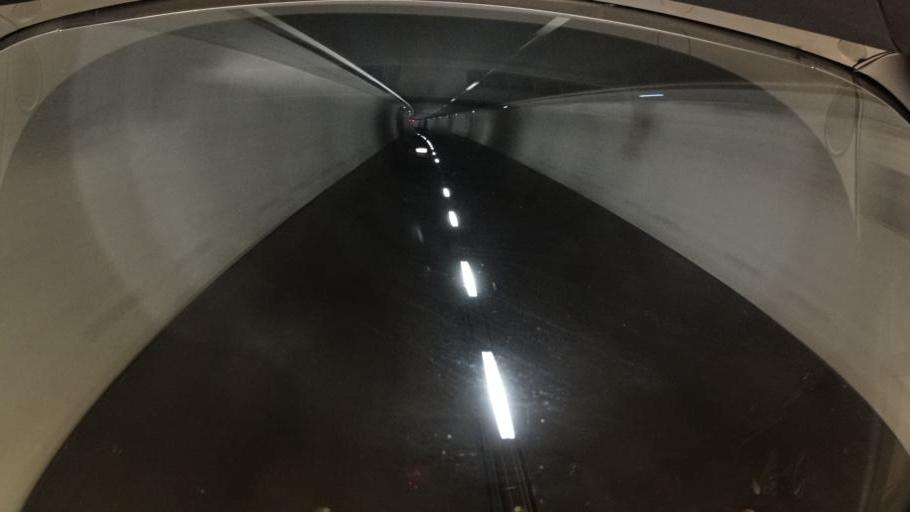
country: NO
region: Sor-Trondelag
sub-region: Trondheim
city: Trondheim
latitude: 63.4281
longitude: 10.5078
